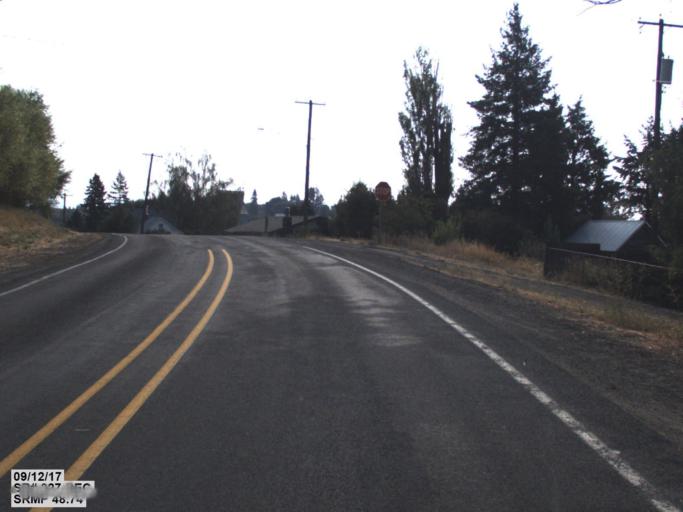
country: US
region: Idaho
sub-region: Benewah County
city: Plummer
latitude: 47.2268
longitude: -117.0780
